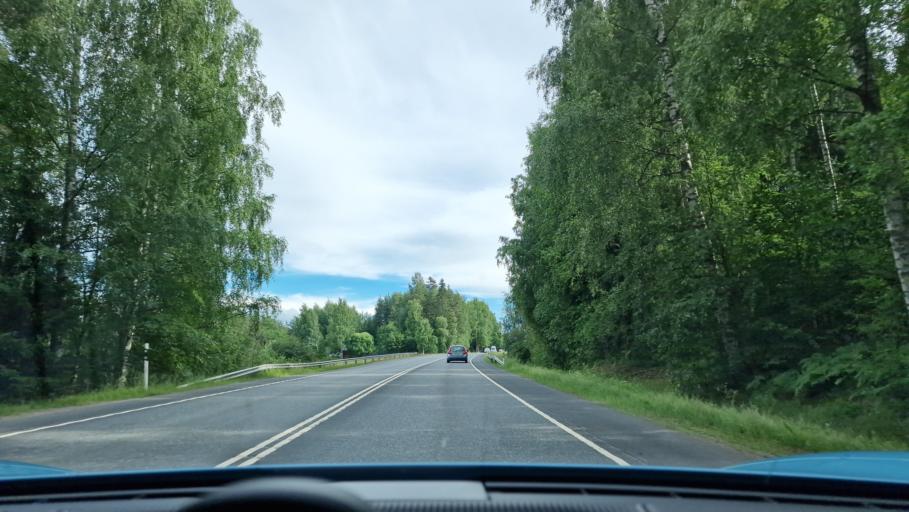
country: FI
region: Pirkanmaa
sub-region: Tampere
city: Paelkaene
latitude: 61.3796
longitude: 24.2435
